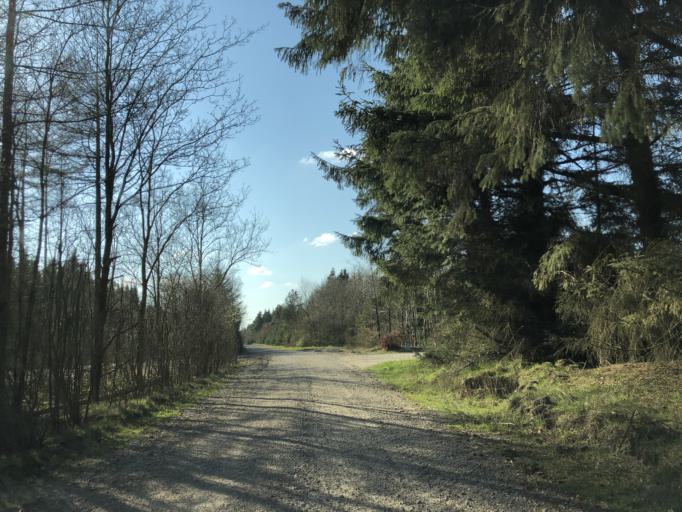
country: DK
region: Central Jutland
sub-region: Holstebro Kommune
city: Ulfborg
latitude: 56.3687
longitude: 8.3065
